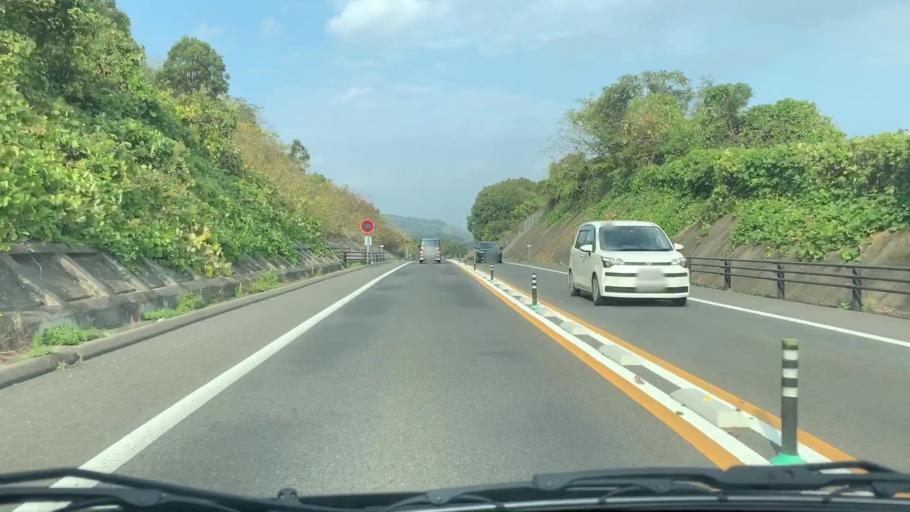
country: JP
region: Nagasaki
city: Sasebo
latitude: 33.0082
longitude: 129.7284
